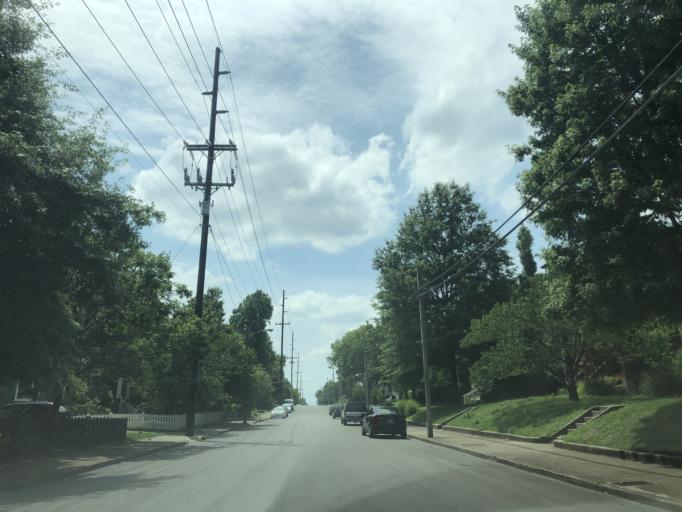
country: US
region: Tennessee
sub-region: Davidson County
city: Nashville
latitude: 36.1782
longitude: -86.7463
